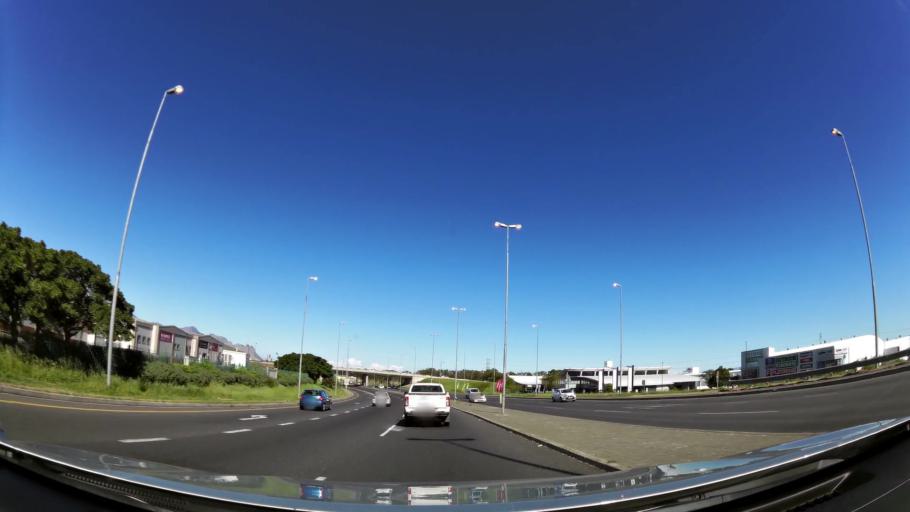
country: ZA
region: Western Cape
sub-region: Cape Winelands District Municipality
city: Stellenbosch
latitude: -34.0796
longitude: 18.8194
